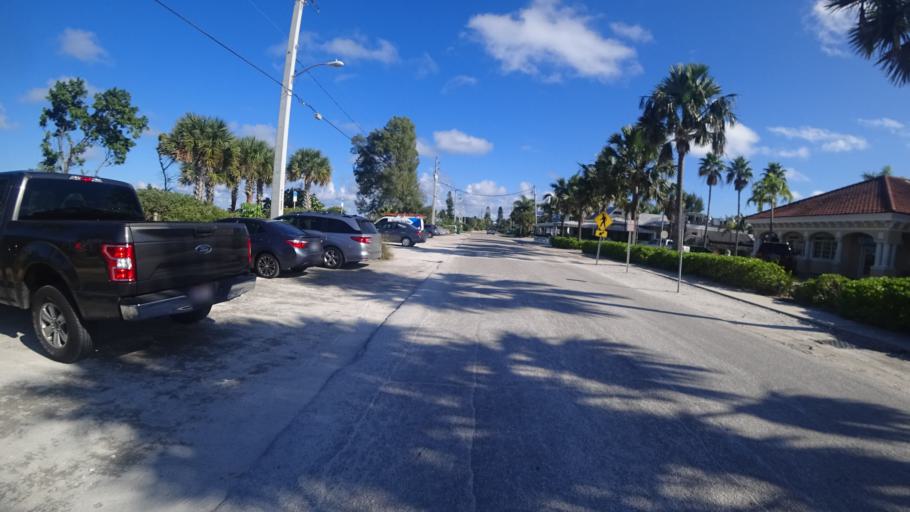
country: US
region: Florida
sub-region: Manatee County
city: Anna Maria
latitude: 27.5326
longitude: -82.7316
